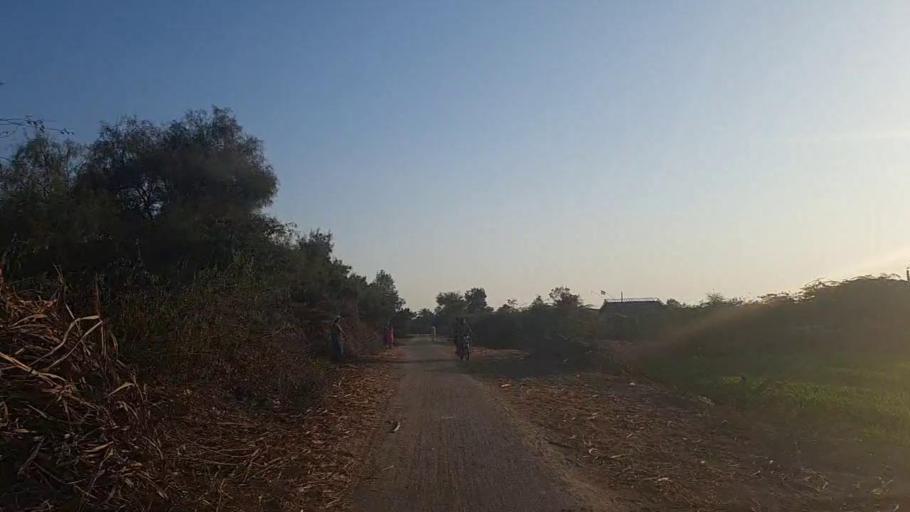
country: PK
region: Sindh
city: Jam Sahib
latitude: 26.3323
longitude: 68.6981
